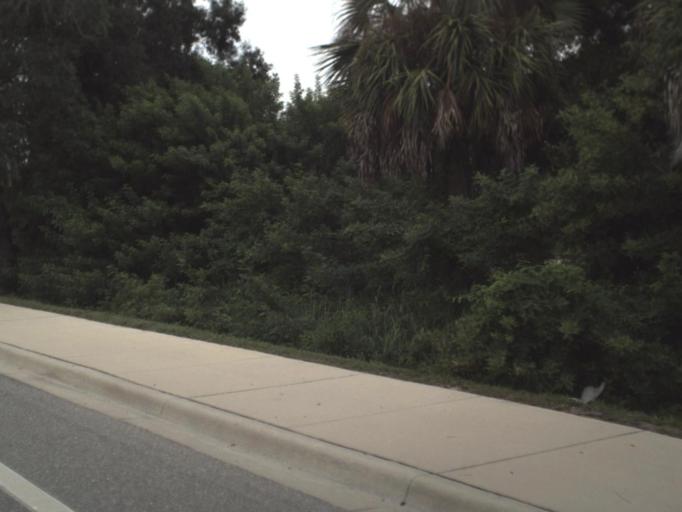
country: US
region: Florida
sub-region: Sarasota County
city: North Sarasota
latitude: 27.3767
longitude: -82.5307
